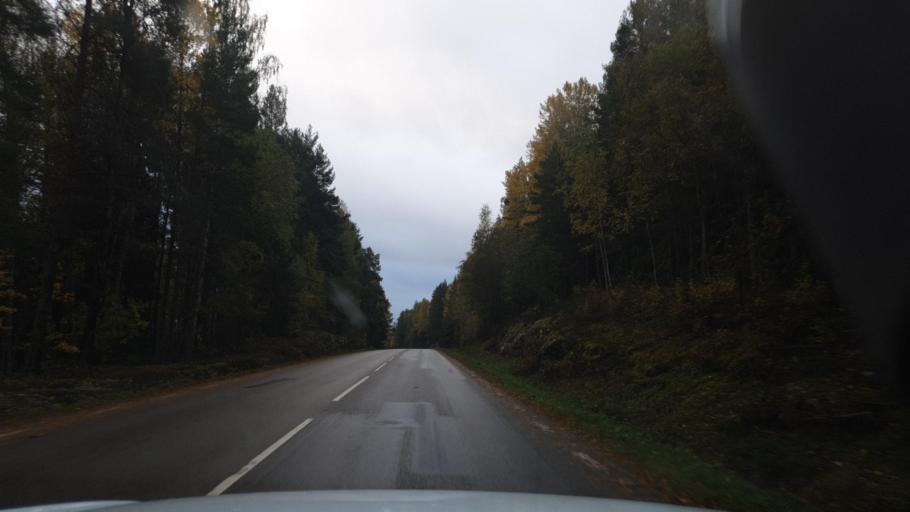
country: SE
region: Vaermland
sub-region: Arvika Kommun
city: Arvika
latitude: 59.7159
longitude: 12.6289
